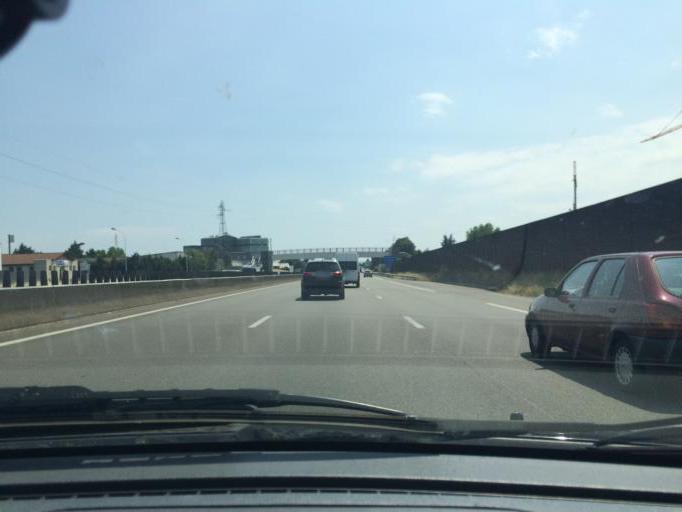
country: FR
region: Rhone-Alpes
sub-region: Departement du Rhone
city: Villefranche-sur-Saone
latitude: 45.9921
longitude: 4.7370
